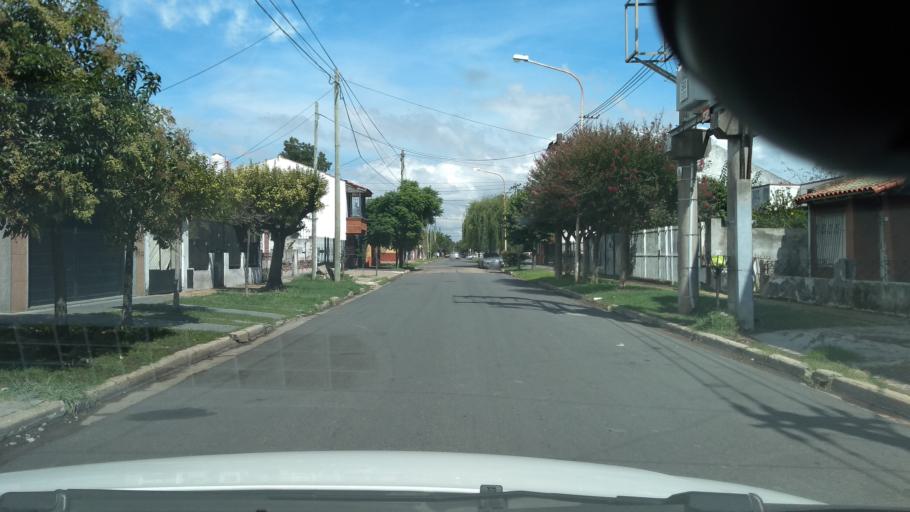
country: AR
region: Buenos Aires
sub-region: Partido de Moron
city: Moron
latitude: -34.6677
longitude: -58.5996
